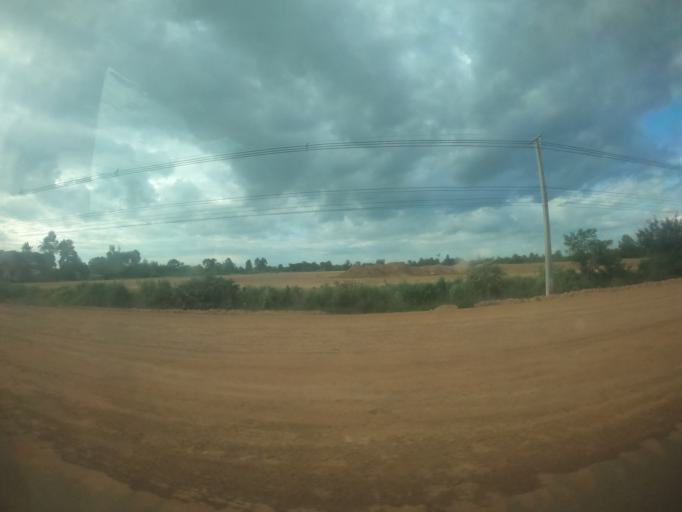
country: TH
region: Surin
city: Kap Choeng
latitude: 14.4599
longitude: 103.6626
